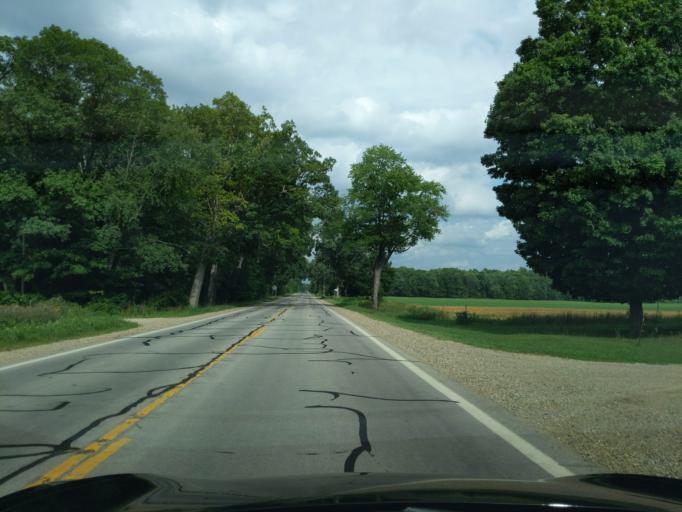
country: US
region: Michigan
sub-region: Eaton County
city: Eaton Rapids
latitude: 42.4150
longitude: -84.6354
